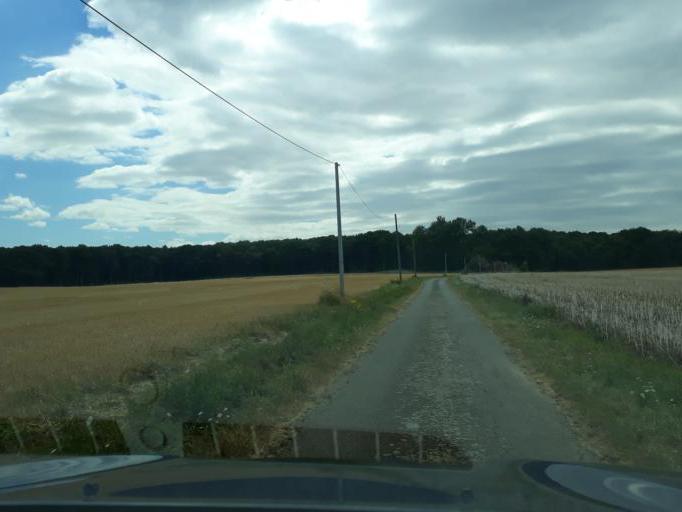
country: FR
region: Centre
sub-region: Departement du Loir-et-Cher
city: Ouzouer-le-Marche
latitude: 47.8821
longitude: 1.4050
